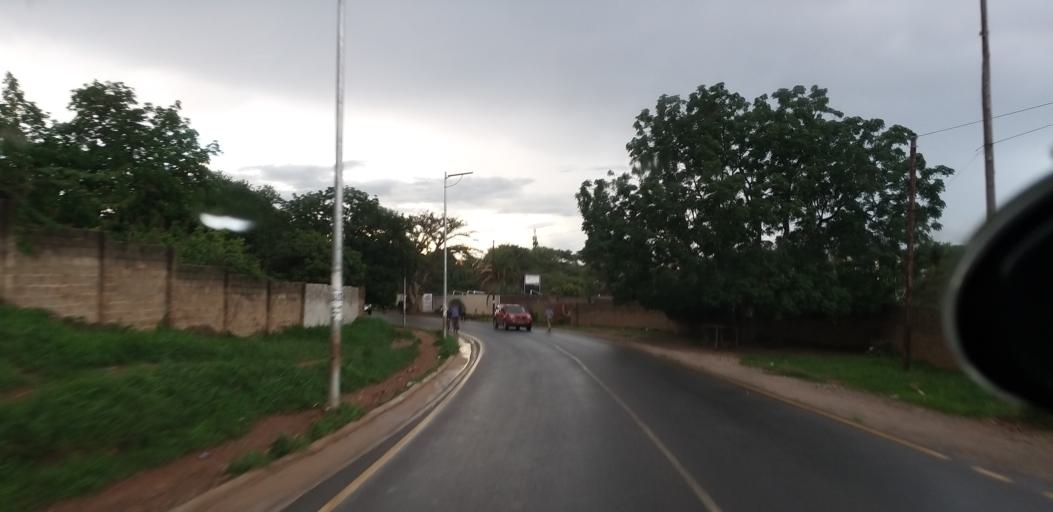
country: ZM
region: Lusaka
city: Lusaka
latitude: -15.4200
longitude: 28.3578
